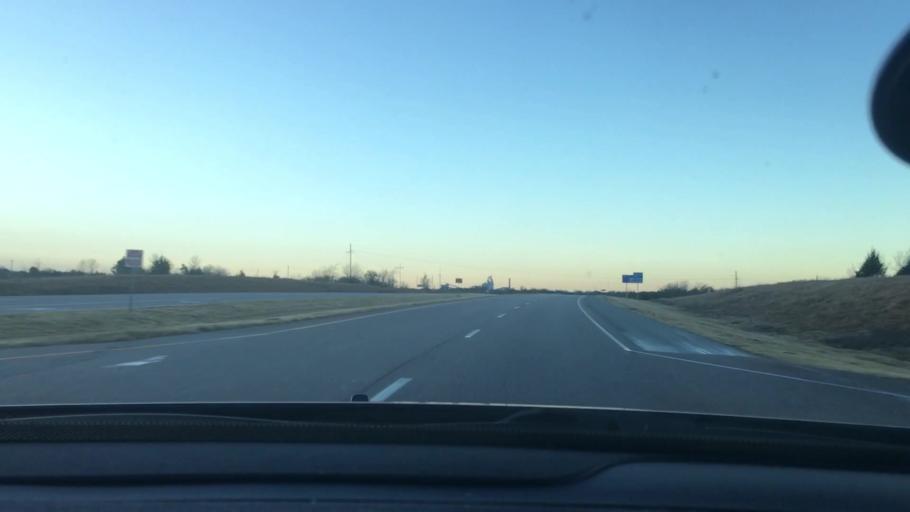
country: US
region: Oklahoma
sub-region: Pontotoc County
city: Ada
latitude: 34.8027
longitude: -96.6953
